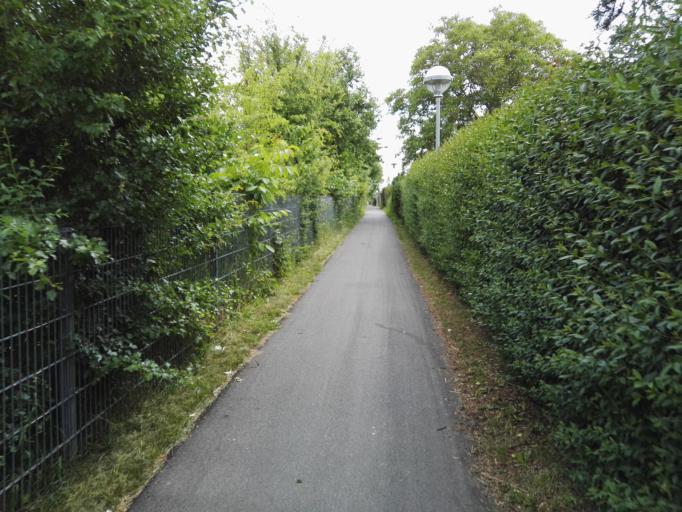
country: DK
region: Capital Region
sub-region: Egedal Kommune
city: Stenlose
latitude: 55.7729
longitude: 12.1877
